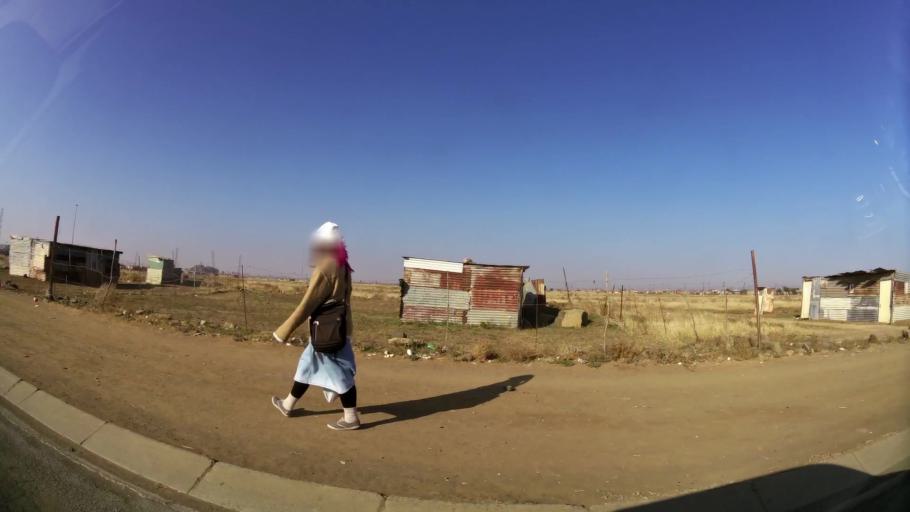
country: ZA
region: Orange Free State
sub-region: Mangaung Metropolitan Municipality
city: Bloemfontein
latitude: -29.2038
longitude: 26.2397
